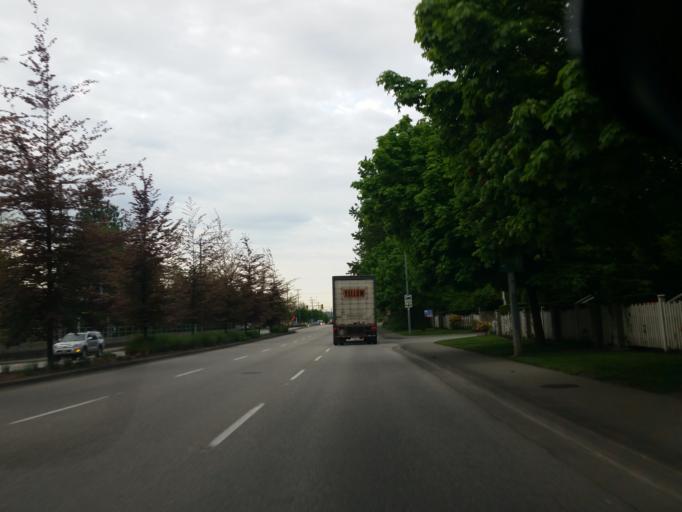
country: CA
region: British Columbia
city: Langley
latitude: 49.1215
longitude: -122.6687
